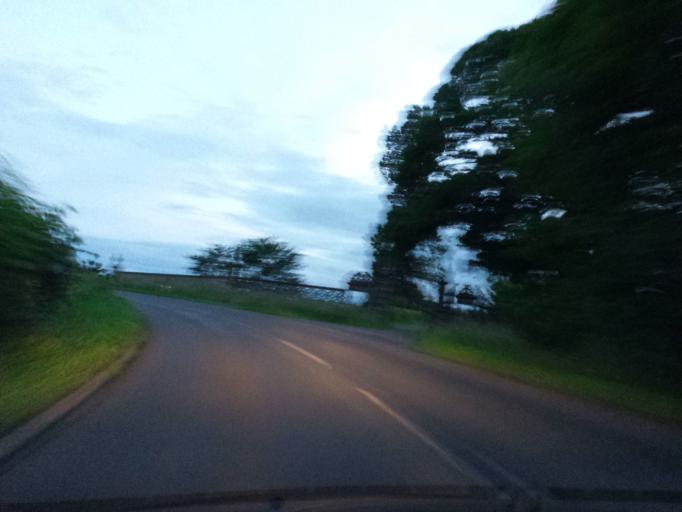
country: GB
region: Scotland
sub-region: The Scottish Borders
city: Duns
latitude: 55.7692
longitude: -2.3714
